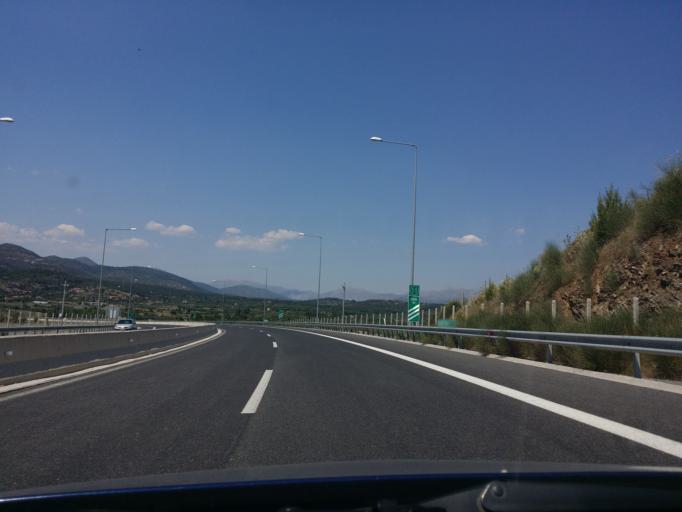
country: GR
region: Peloponnese
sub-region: Nomos Arkadias
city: Tripoli
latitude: 37.4534
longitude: 22.3280
